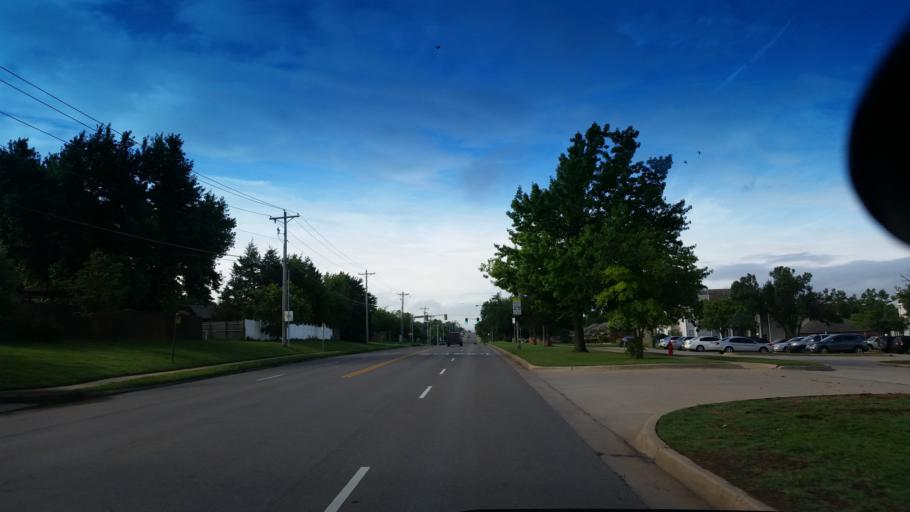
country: US
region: Oklahoma
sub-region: Oklahoma County
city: Edmond
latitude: 35.6623
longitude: -97.4961
